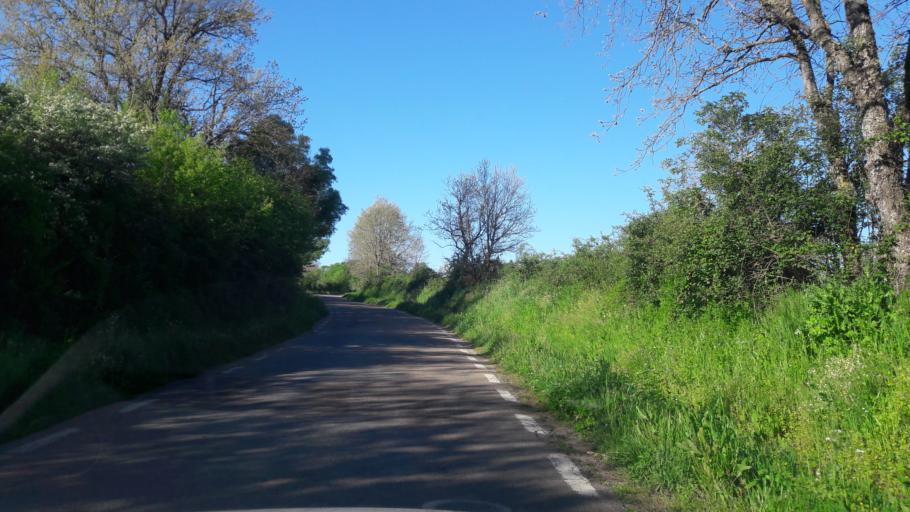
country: ES
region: Castille and Leon
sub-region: Provincia de Salamanca
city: Endrinal
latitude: 40.5864
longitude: -5.8047
